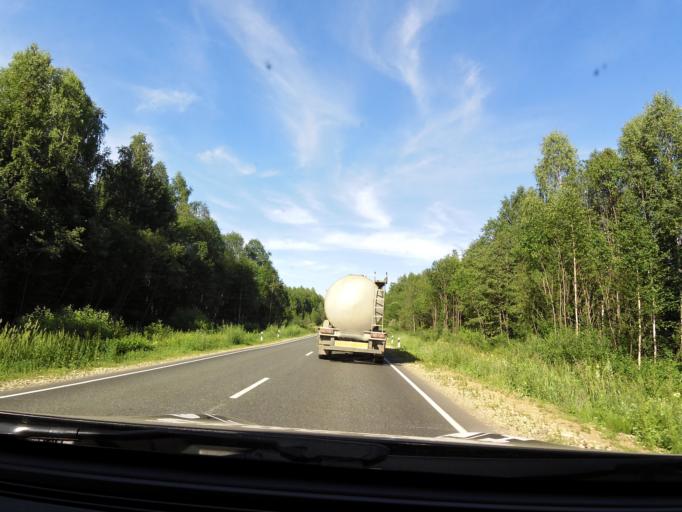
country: RU
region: Kirov
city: Belaya Kholunitsa
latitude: 58.9004
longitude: 50.9306
